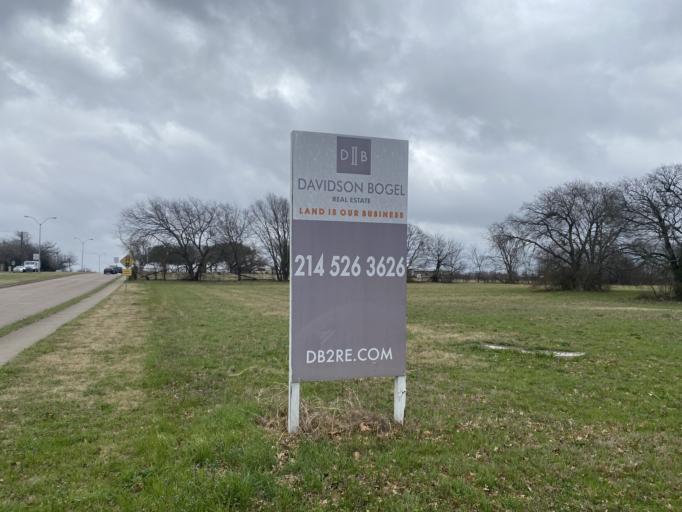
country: US
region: Texas
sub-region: Dallas County
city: Lancaster
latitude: 32.6041
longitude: -96.7943
